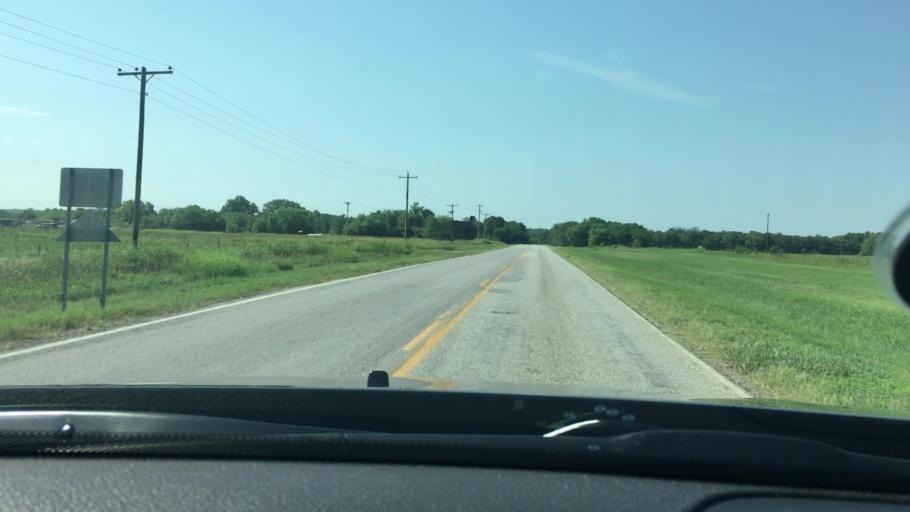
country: US
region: Oklahoma
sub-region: Johnston County
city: Tishomingo
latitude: 34.3409
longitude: -96.4216
